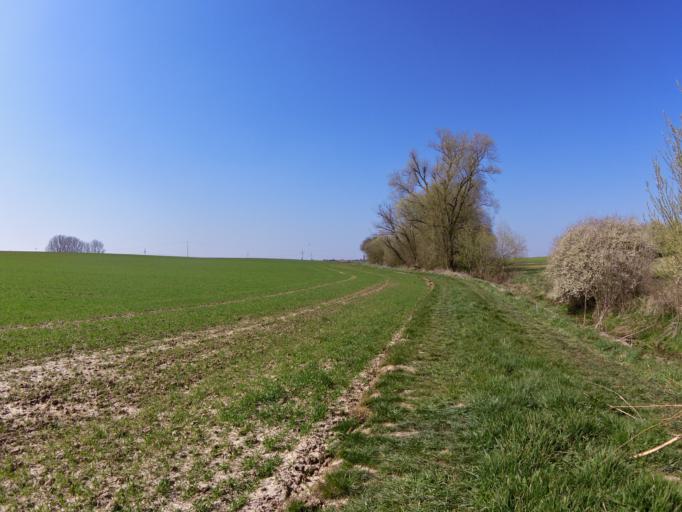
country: DE
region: Bavaria
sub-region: Regierungsbezirk Unterfranken
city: Biebelried
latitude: 49.7442
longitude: 10.0920
